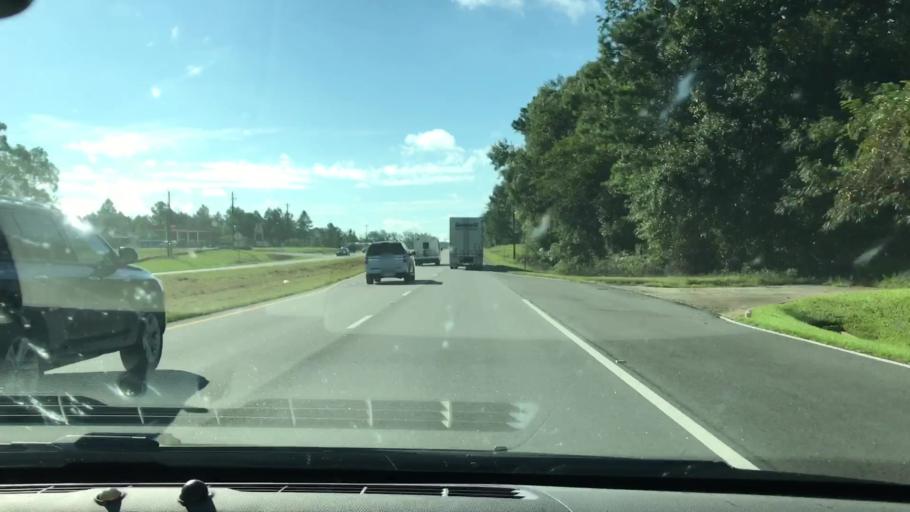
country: US
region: Georgia
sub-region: Dougherty County
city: Albany
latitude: 31.6393
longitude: -84.2508
